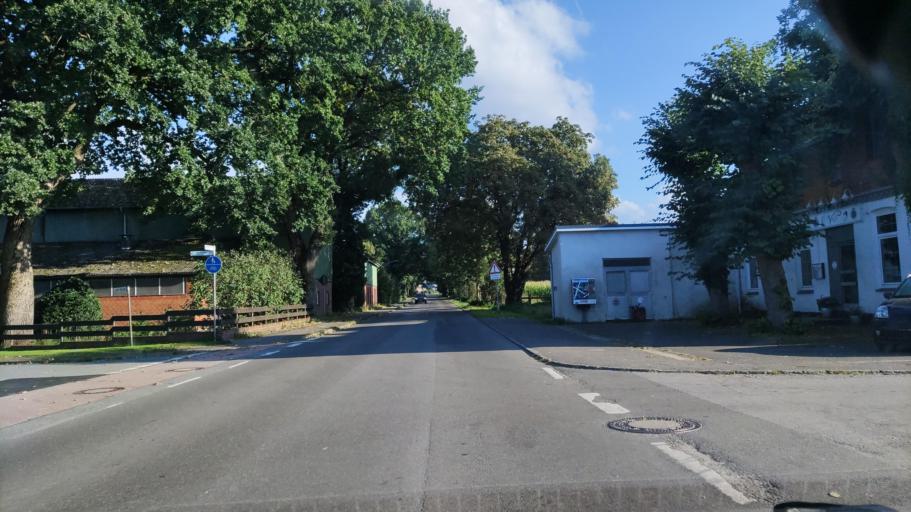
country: DE
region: Schleswig-Holstein
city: Armstedt
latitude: 53.9712
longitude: 9.8470
